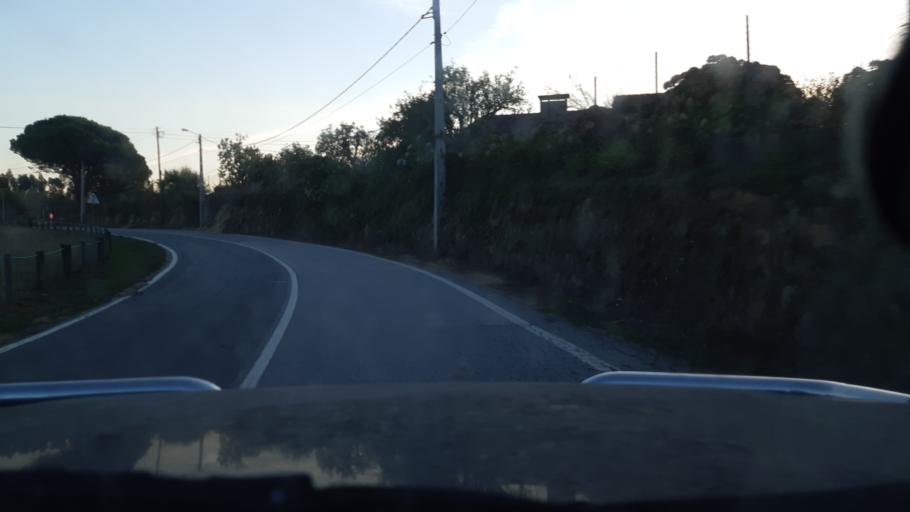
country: PT
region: Aveiro
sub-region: Agueda
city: Aguada de Cima
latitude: 40.5691
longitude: -8.3676
